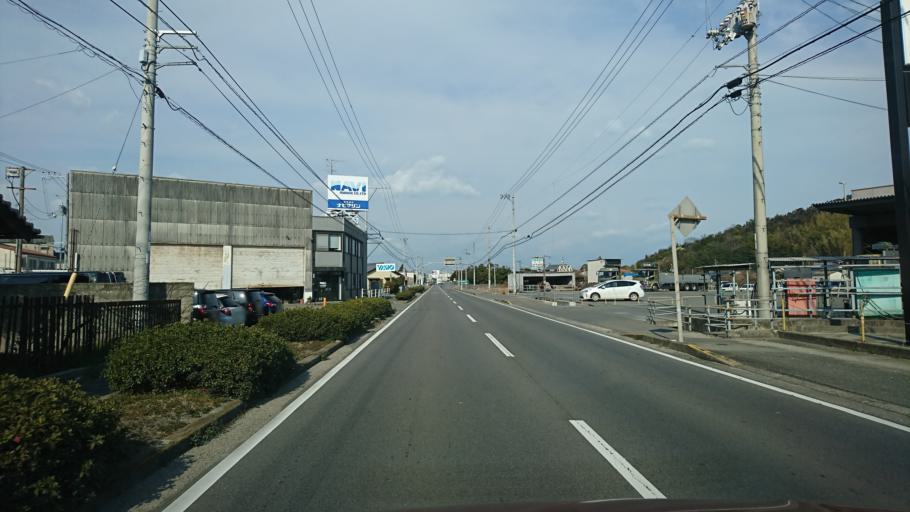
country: JP
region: Ehime
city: Saijo
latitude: 34.0087
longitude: 133.0386
